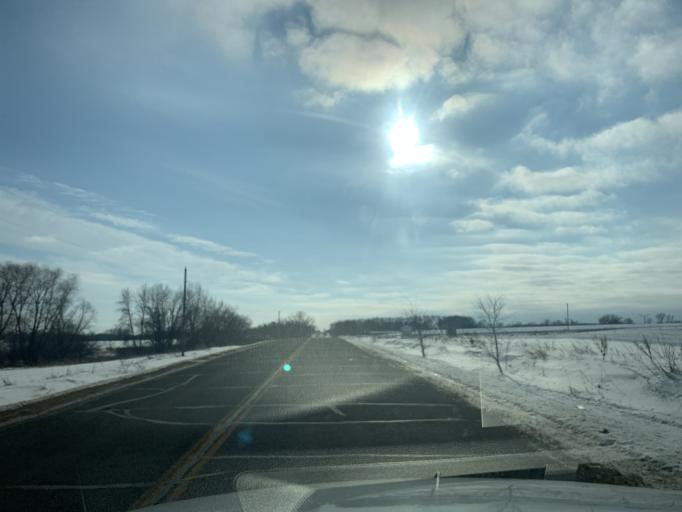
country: US
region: Minnesota
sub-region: Wright County
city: Buffalo
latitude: 45.1953
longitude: -93.8272
